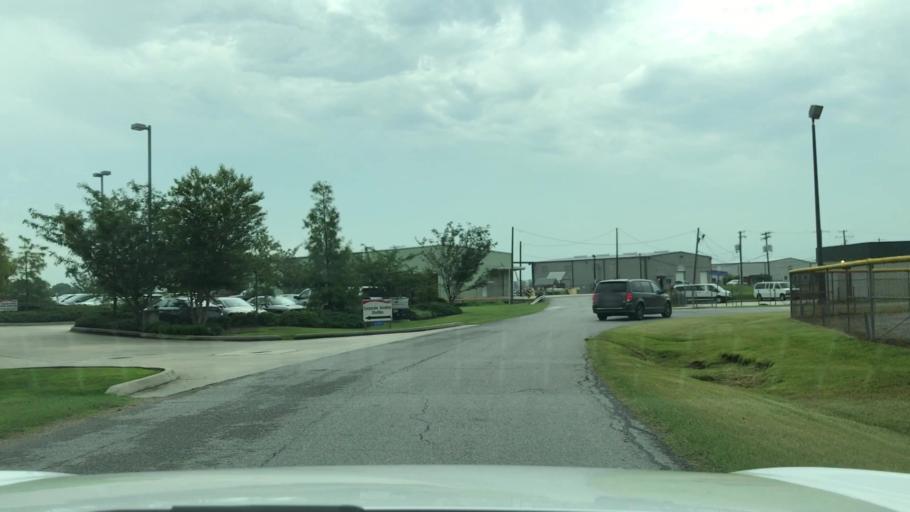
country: US
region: Louisiana
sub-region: East Baton Rouge Parish
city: Brownsfield
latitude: 30.5359
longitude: -91.1602
